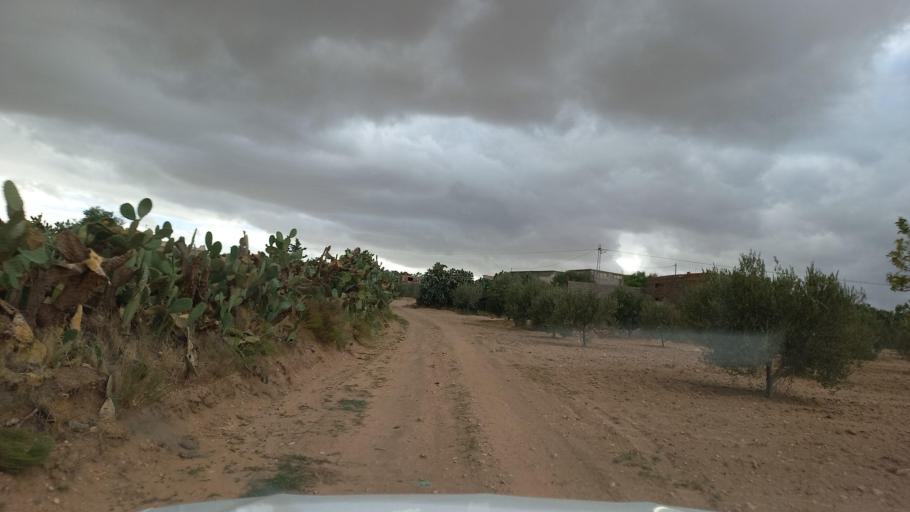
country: TN
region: Al Qasrayn
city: Kasserine
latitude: 35.2753
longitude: 8.9535
